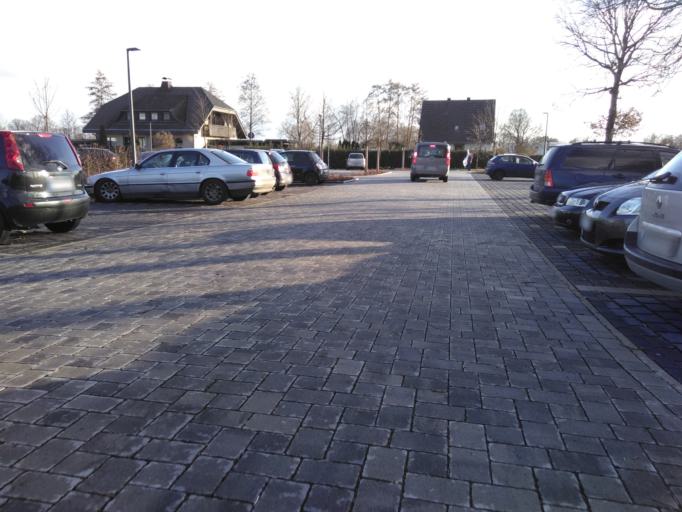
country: DE
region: North Rhine-Westphalia
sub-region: Regierungsbezirk Detmold
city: Verl
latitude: 51.8687
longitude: 8.4723
